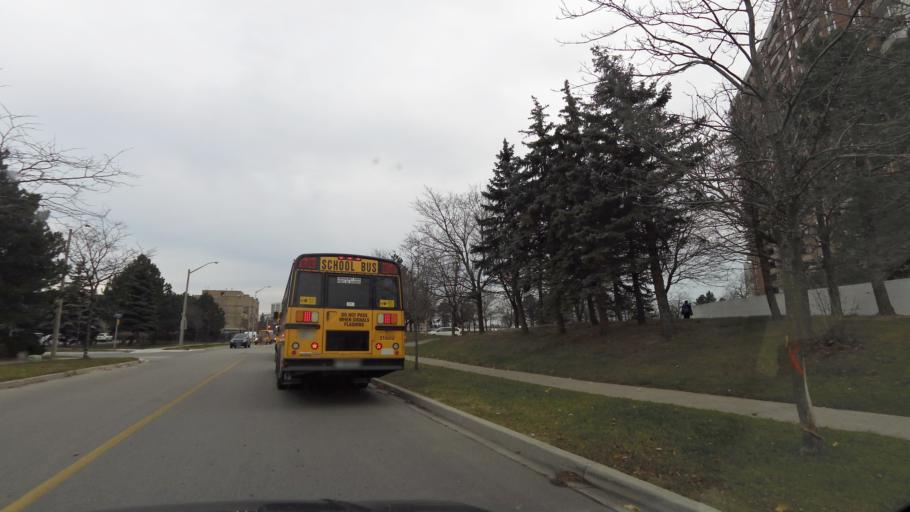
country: CA
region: Ontario
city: Etobicoke
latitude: 43.6283
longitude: -79.6070
